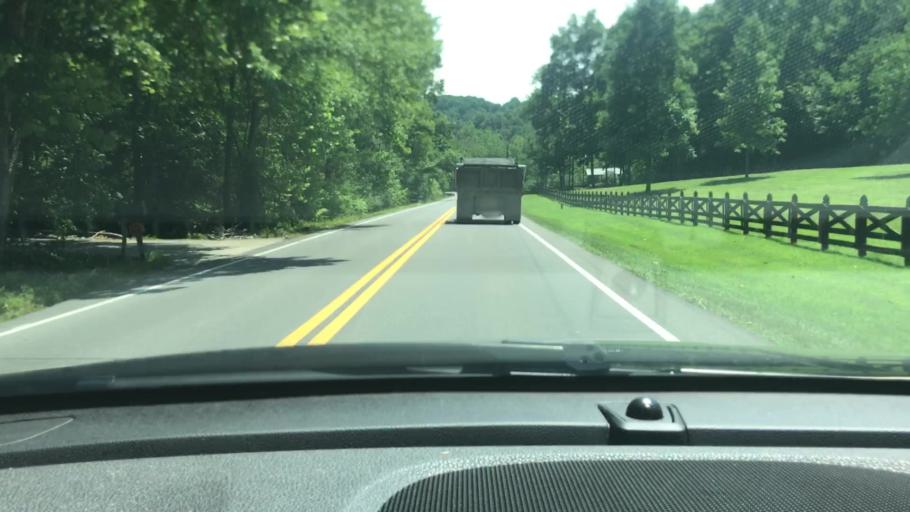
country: US
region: Tennessee
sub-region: Sumner County
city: White House
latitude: 36.4285
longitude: -86.6587
